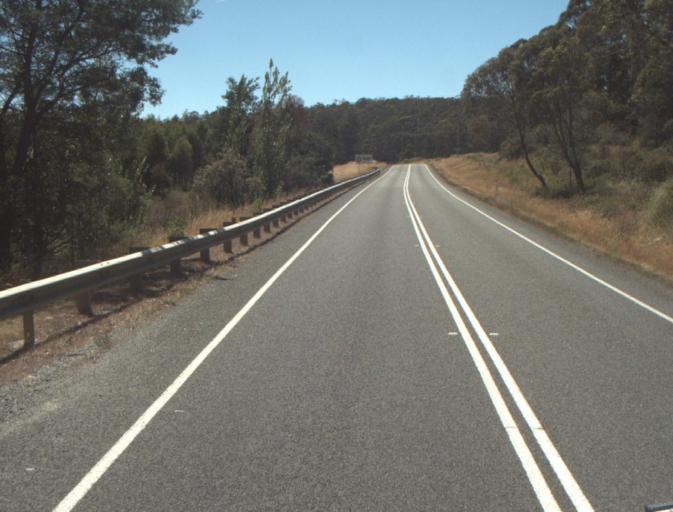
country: AU
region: Tasmania
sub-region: Launceston
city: Newstead
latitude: -41.3863
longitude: 147.3071
